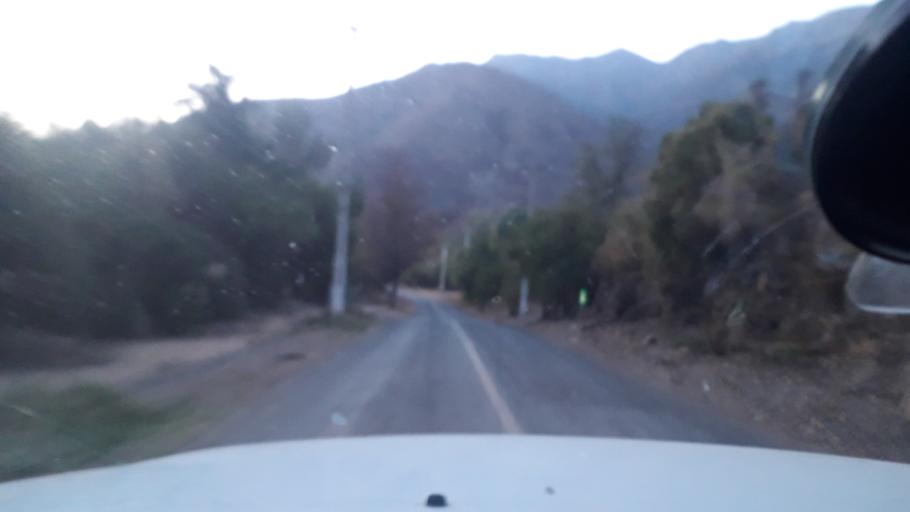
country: CL
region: Valparaiso
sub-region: Provincia de Marga Marga
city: Limache
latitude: -33.1701
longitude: -71.1334
